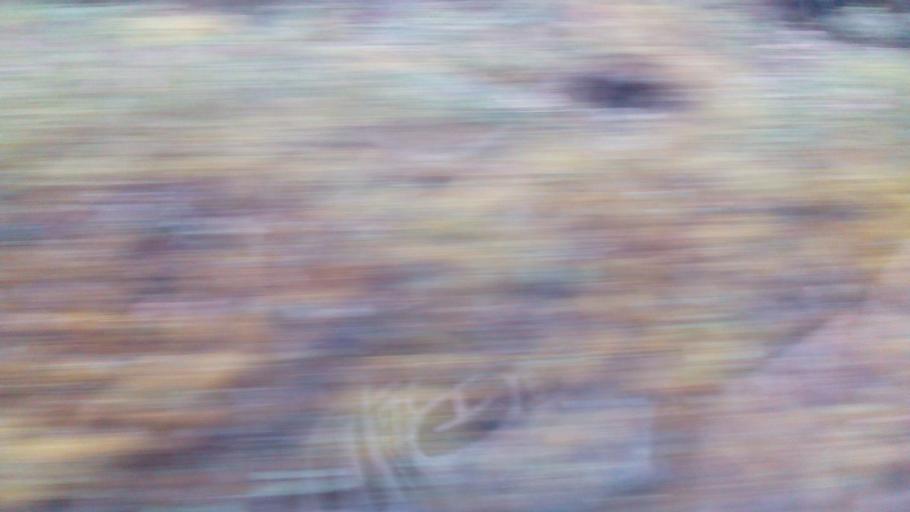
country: TW
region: Taiwan
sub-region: Hualien
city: Hualian
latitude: 24.3964
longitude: 121.3585
